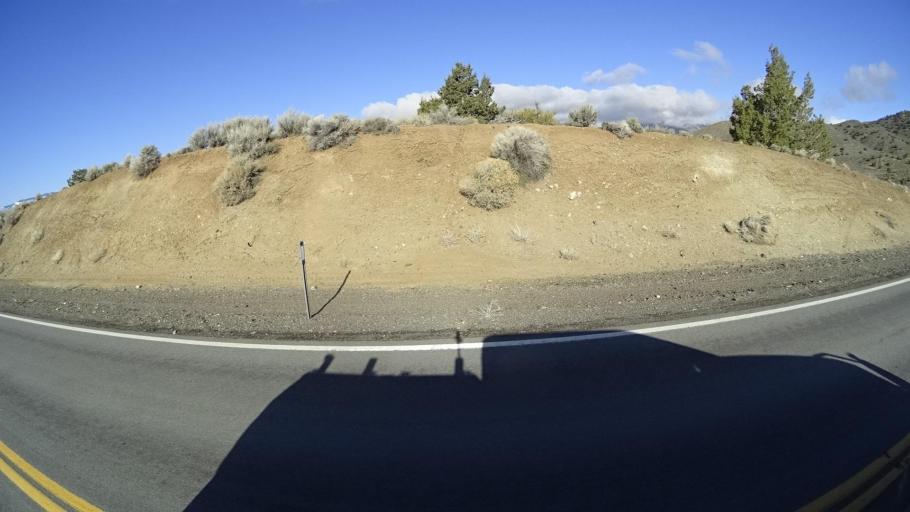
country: US
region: Nevada
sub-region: Washoe County
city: Cold Springs
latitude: 39.6974
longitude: -119.9110
